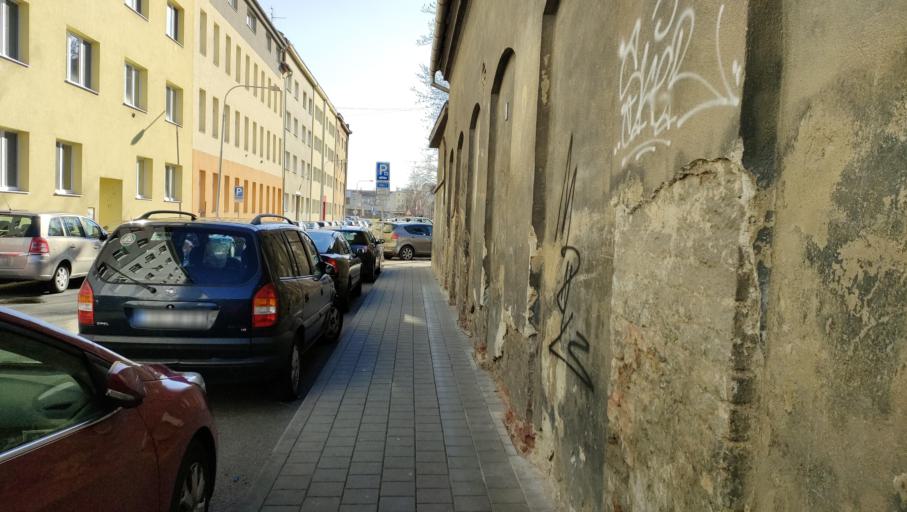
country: CZ
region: South Moravian
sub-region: Mesto Brno
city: Brno
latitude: 49.1975
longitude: 16.6240
